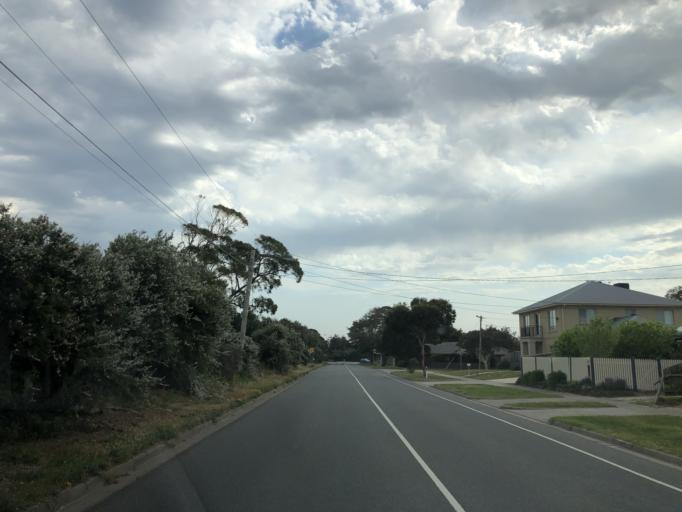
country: AU
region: Victoria
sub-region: Kingston
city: Carrum
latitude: -38.0838
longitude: 145.1276
